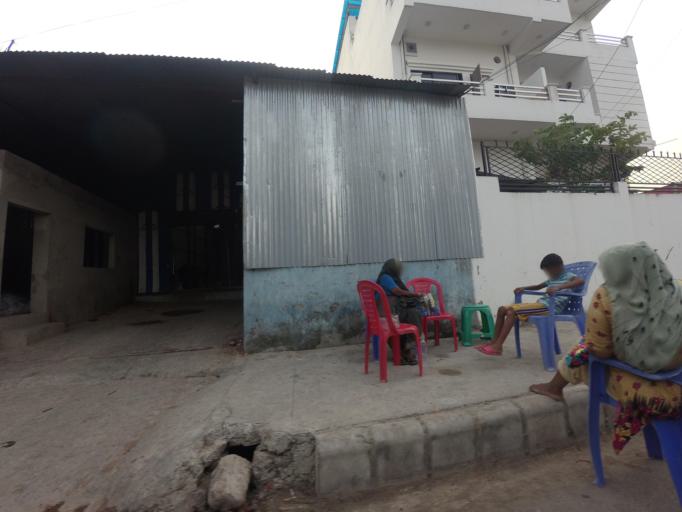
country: NP
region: Western Region
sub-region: Lumbini Zone
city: Bhairahawa
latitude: 27.5075
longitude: 83.4474
